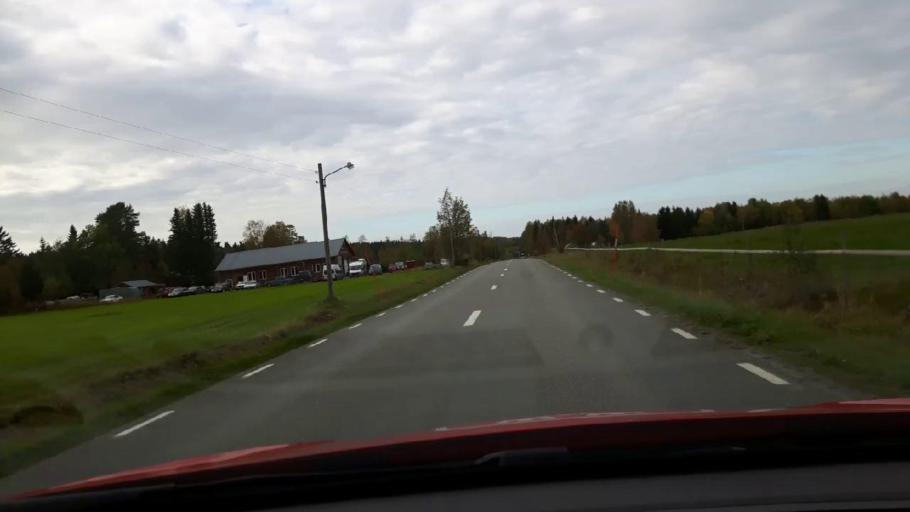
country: SE
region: Jaemtland
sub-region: Krokoms Kommun
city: Krokom
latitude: 63.1656
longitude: 14.1168
